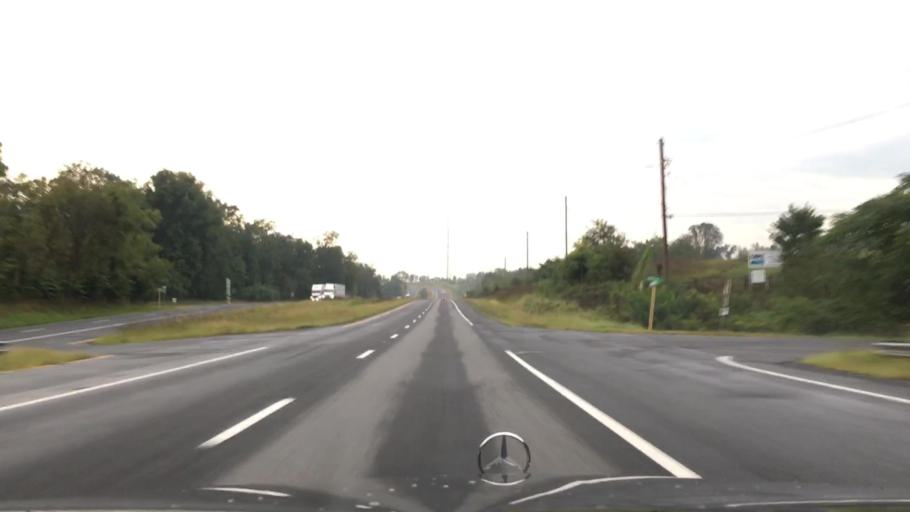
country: US
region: West Virginia
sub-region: Morgan County
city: Berkeley Springs
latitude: 39.4337
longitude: -78.3100
